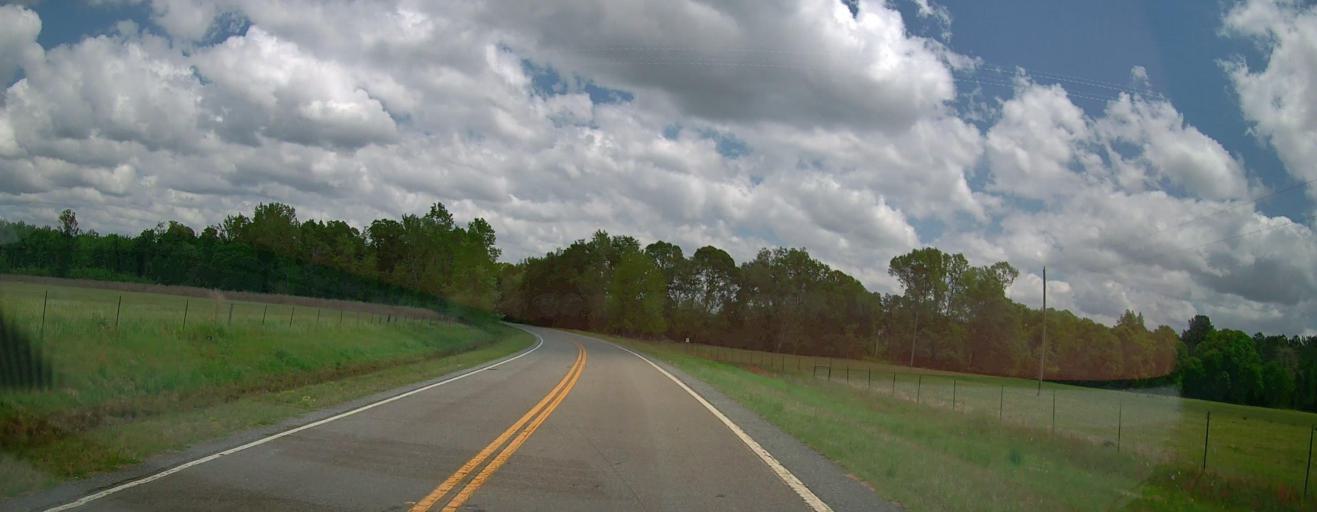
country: US
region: Georgia
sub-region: Dodge County
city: Chester
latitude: 32.5460
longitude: -83.1795
